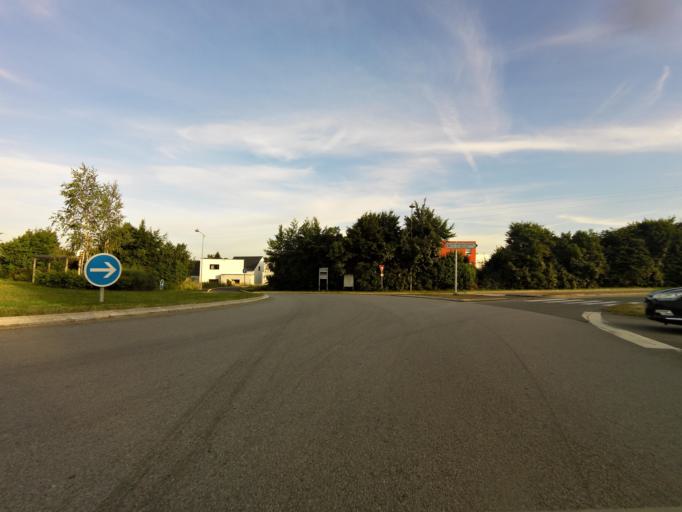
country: FR
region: Brittany
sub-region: Departement du Morbihan
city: Ploeren
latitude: 47.6597
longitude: -2.8594
